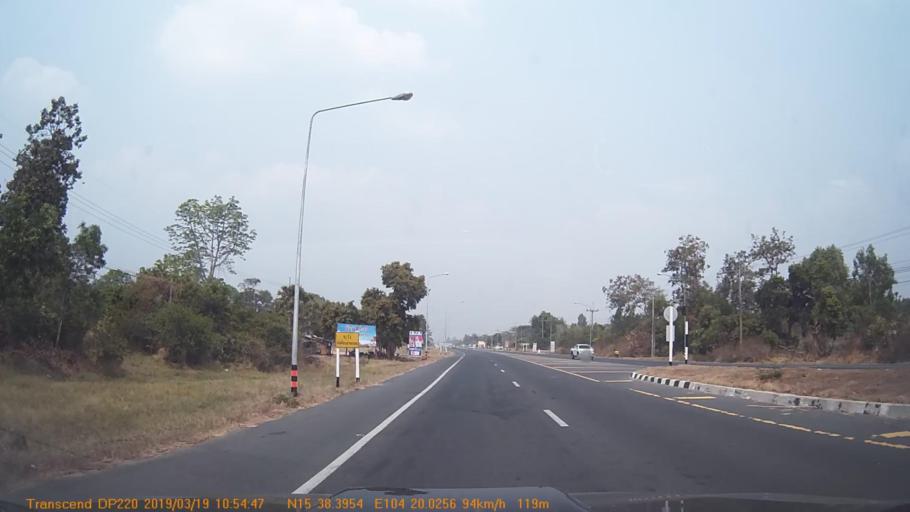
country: TH
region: Yasothon
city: Kham Khuean Kaeo
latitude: 15.6402
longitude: 104.3334
